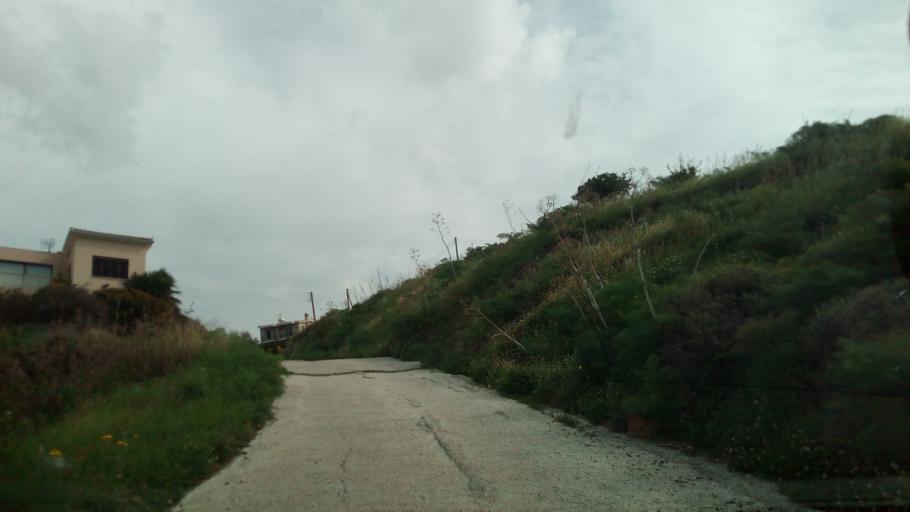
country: CY
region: Pafos
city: Mesogi
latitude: 34.7967
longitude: 32.4741
